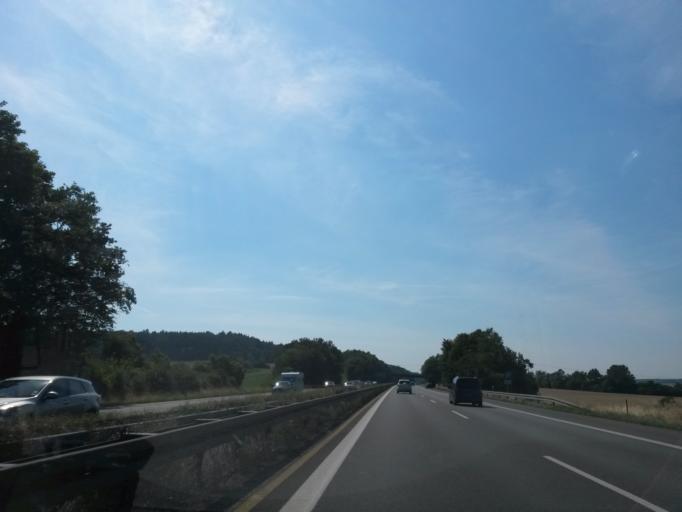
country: DE
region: Bavaria
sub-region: Regierungsbezirk Unterfranken
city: Geiselwind
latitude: 49.7635
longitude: 10.5297
